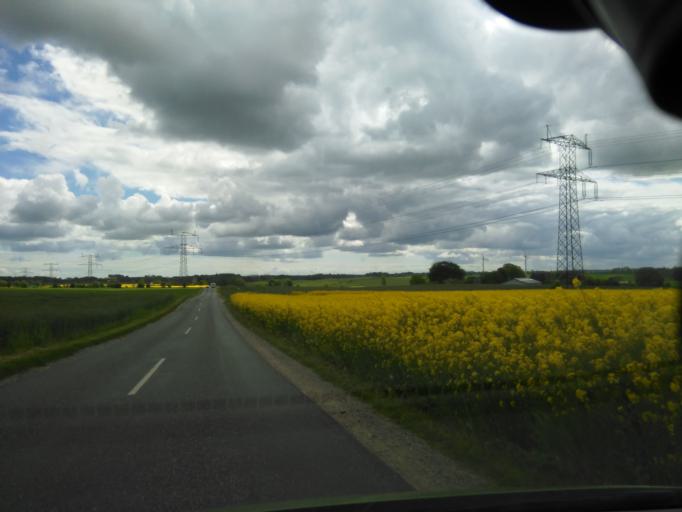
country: DK
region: Central Jutland
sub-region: Arhus Kommune
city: Kolt
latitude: 56.0829
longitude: 10.0825
